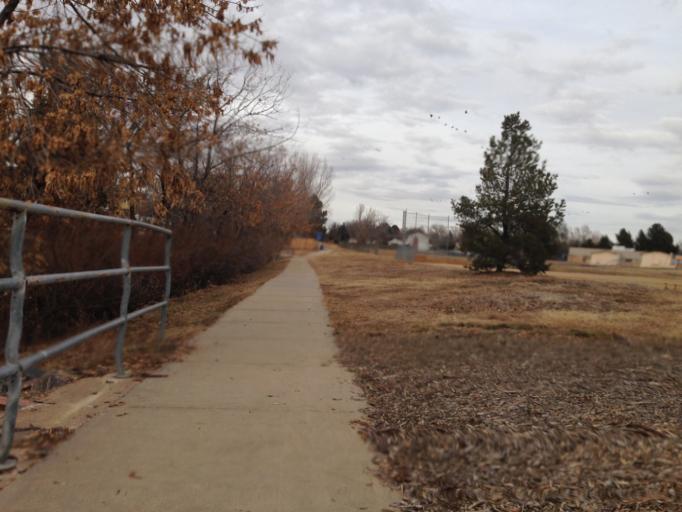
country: US
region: Colorado
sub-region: Adams County
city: Westminster
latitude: 39.8476
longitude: -105.0628
